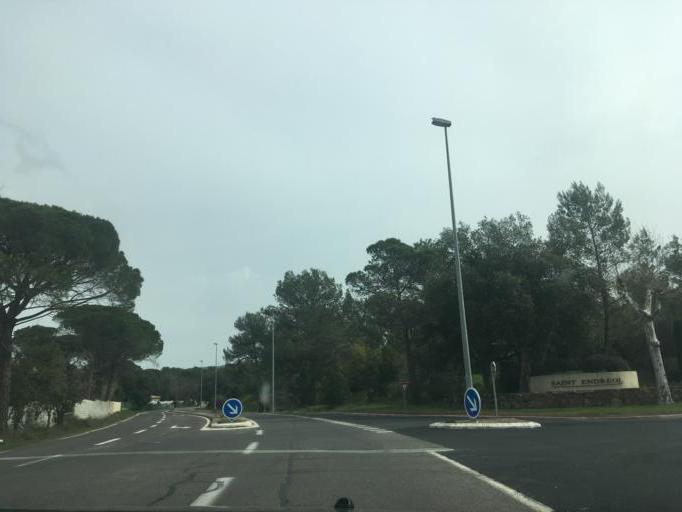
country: FR
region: Provence-Alpes-Cote d'Azur
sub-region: Departement du Var
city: Le Muy
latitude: 43.4979
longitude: 6.5782
